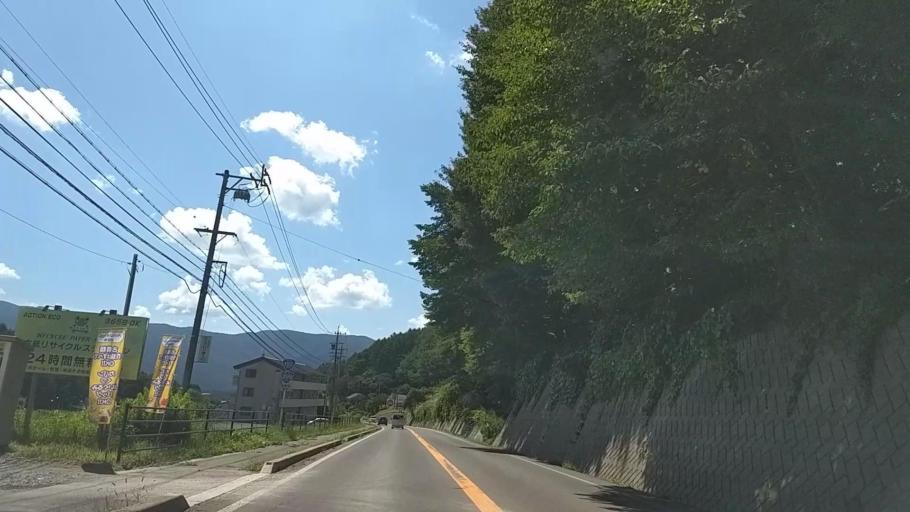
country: JP
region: Nagano
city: Chino
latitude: 36.0125
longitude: 138.1835
